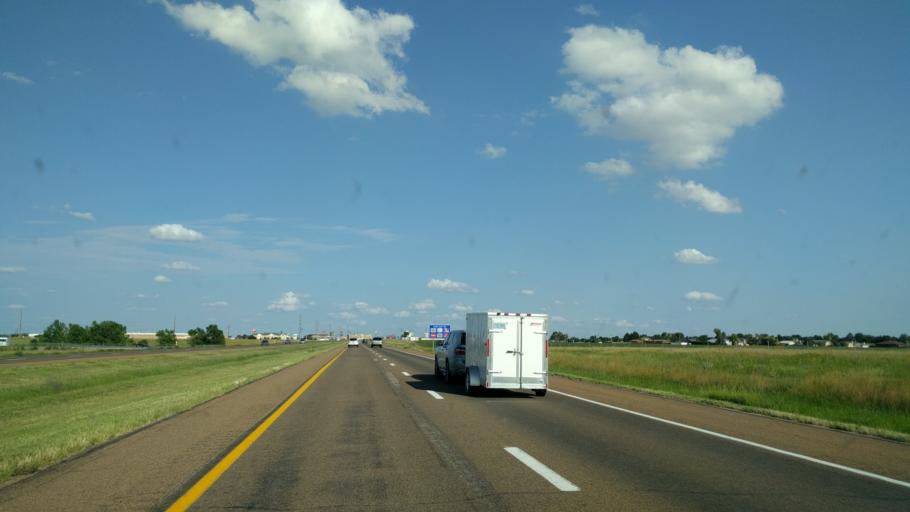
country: US
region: Kansas
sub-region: Ellis County
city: Hays
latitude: 38.9047
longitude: -99.3332
